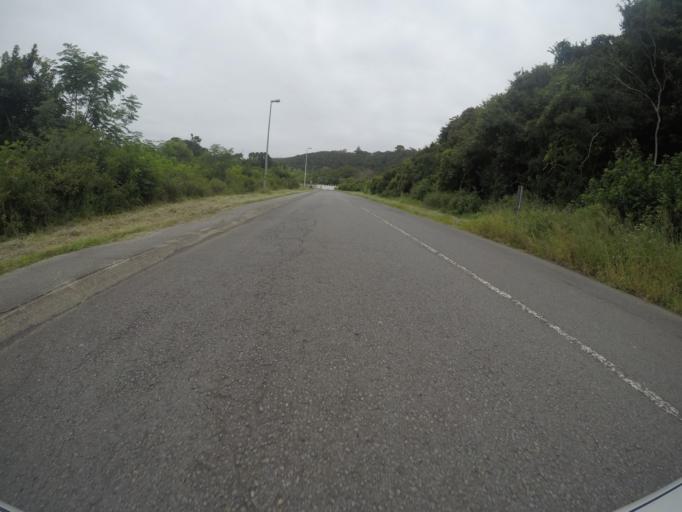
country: ZA
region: Eastern Cape
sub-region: Buffalo City Metropolitan Municipality
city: East London
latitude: -32.9767
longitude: 27.9333
